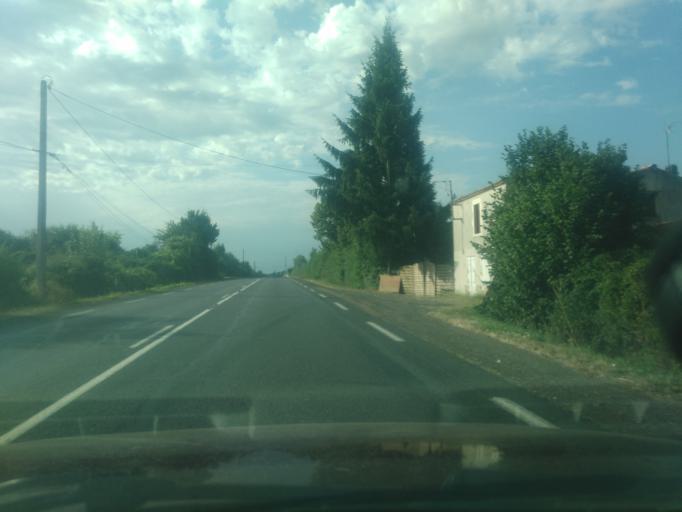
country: FR
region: Pays de la Loire
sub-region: Departement de la Vendee
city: Sainte-Cecile
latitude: 46.7555
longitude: -1.0984
